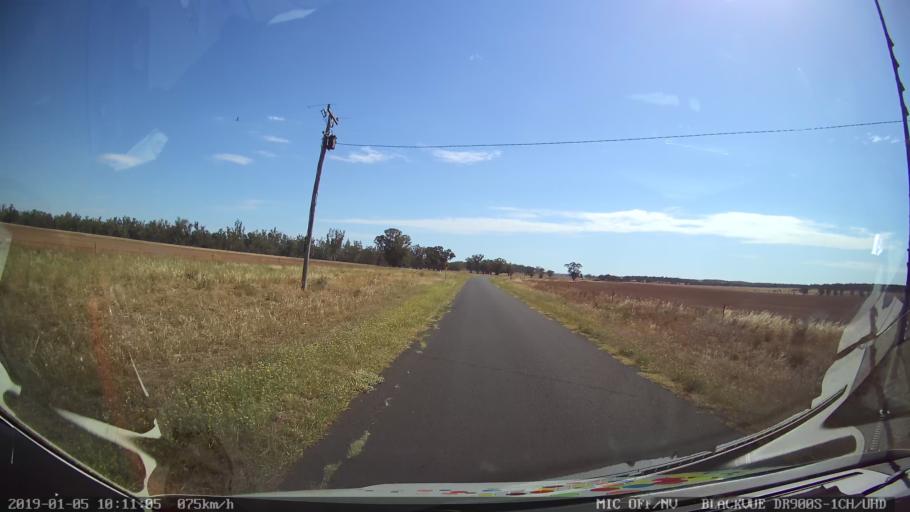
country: AU
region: New South Wales
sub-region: Gilgandra
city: Gilgandra
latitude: -31.6159
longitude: 148.8978
